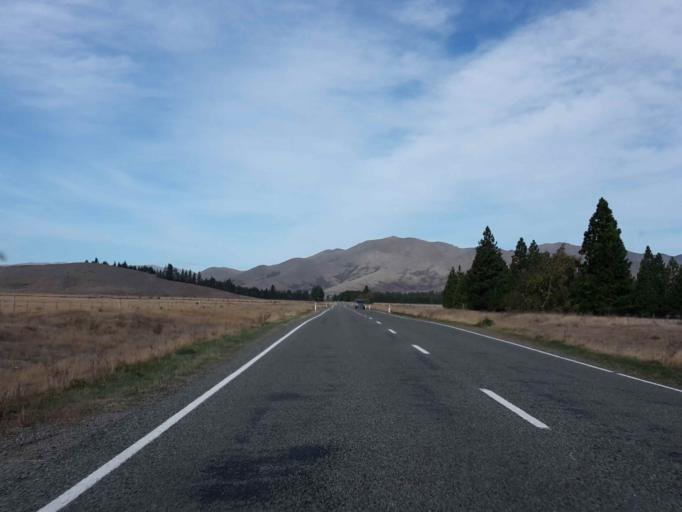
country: NZ
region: Canterbury
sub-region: Timaru District
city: Pleasant Point
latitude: -44.0766
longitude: 170.5249
